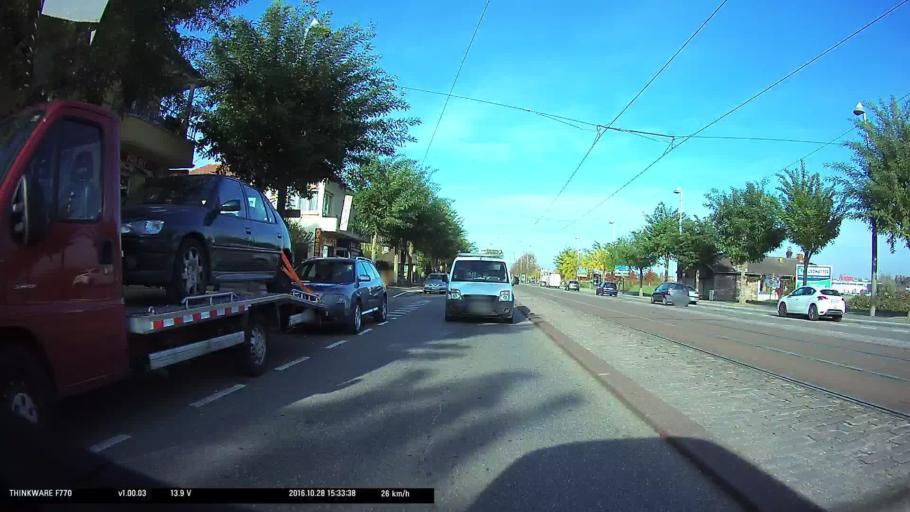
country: FR
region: Alsace
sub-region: Departement du Bas-Rhin
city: Illkirch-Graffenstaden
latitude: 48.5409
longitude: 7.7348
